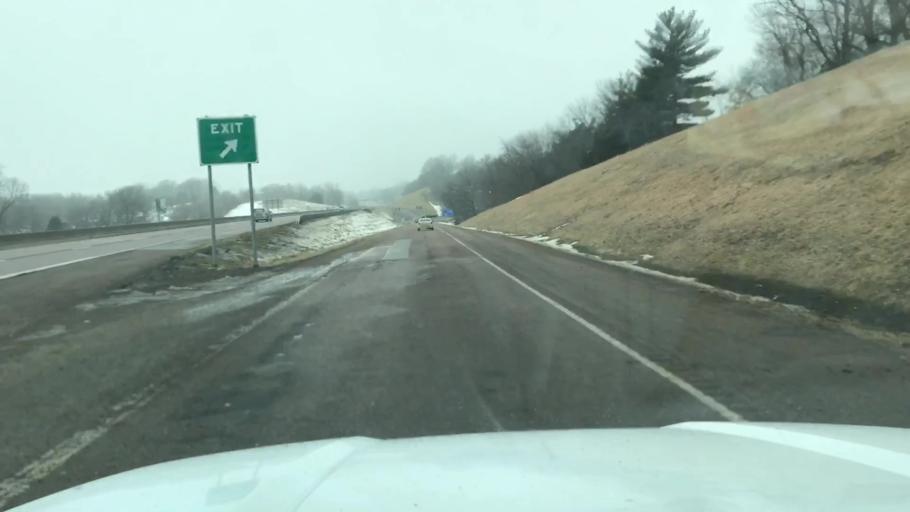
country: US
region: Missouri
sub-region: Buchanan County
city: Saint Joseph
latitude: 39.7469
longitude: -94.7977
